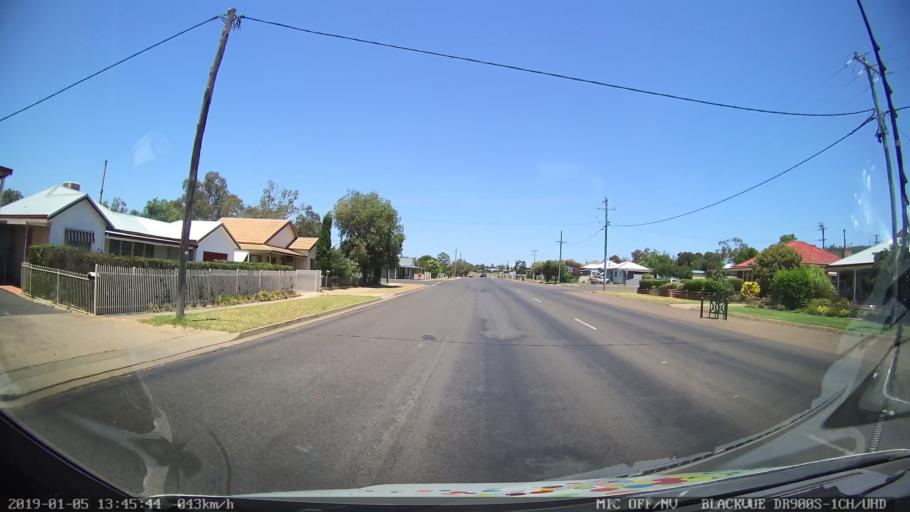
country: AU
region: New South Wales
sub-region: Gunnedah
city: Gunnedah
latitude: -30.9844
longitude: 150.2634
